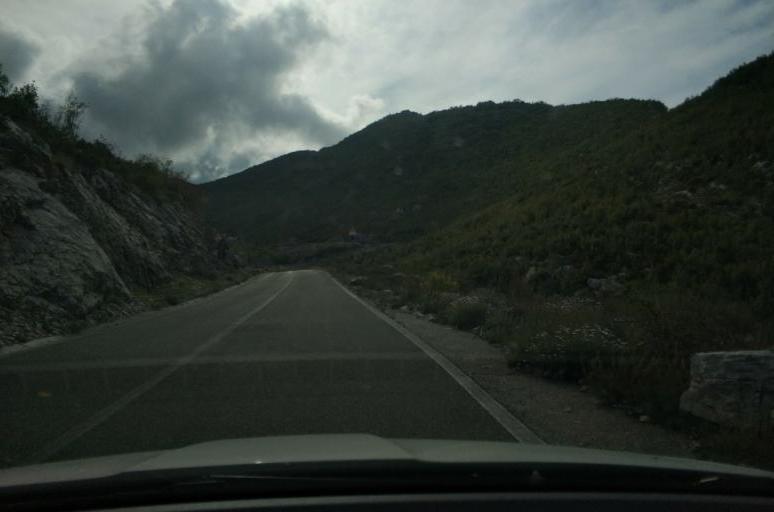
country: AL
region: Durres
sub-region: Rrethi i Krujes
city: Kruje
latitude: 41.5289
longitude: 19.7963
